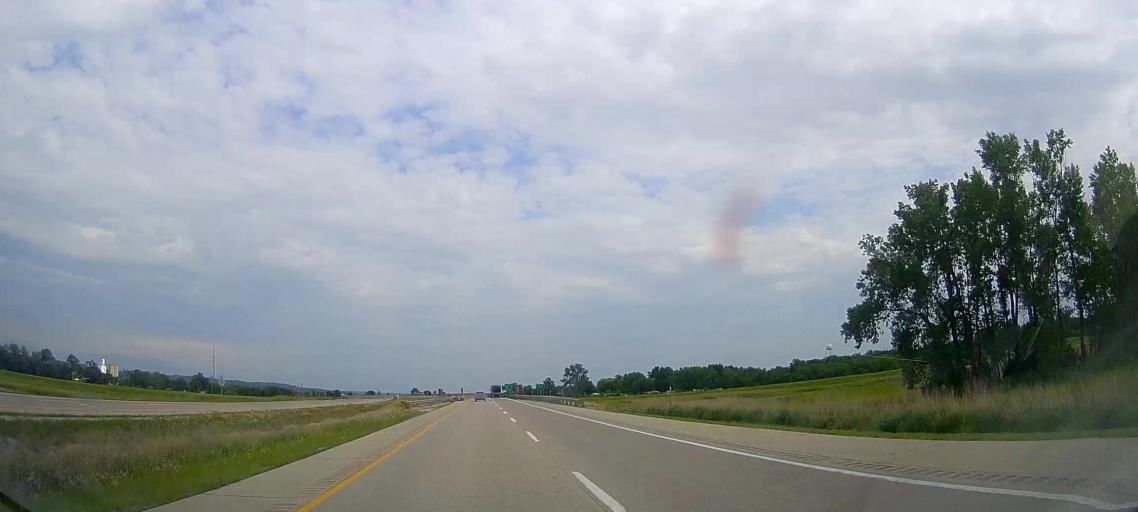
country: US
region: Nebraska
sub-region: Burt County
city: Tekamah
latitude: 41.8077
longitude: -96.0608
